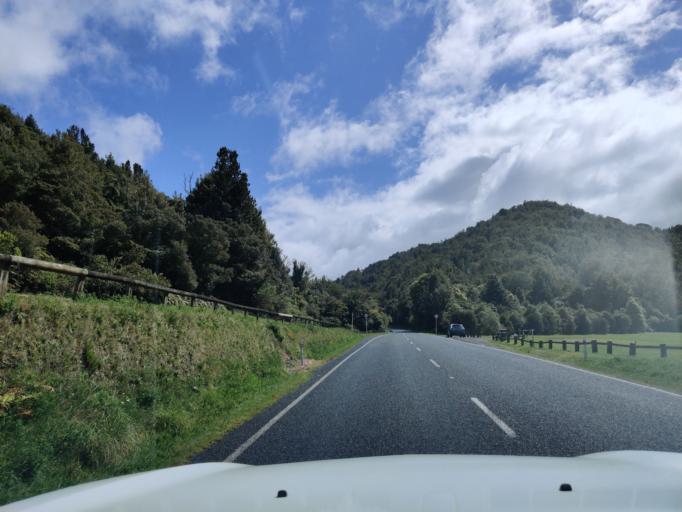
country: NZ
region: Bay of Plenty
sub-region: Rotorua District
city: Rotorua
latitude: -38.1853
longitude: 176.3283
